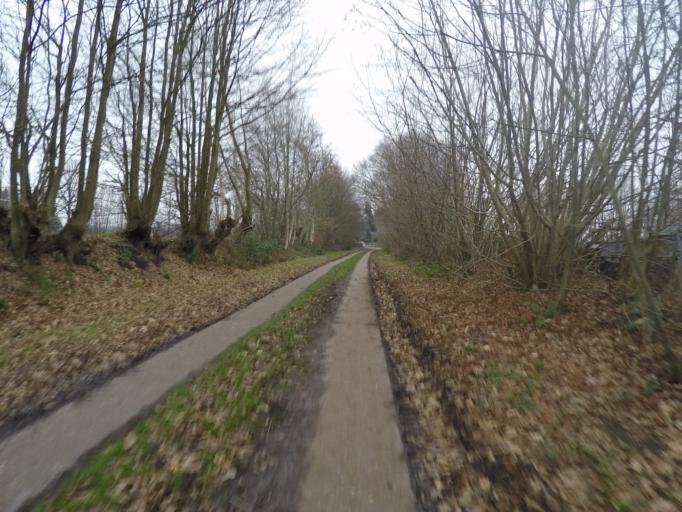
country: DE
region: Schleswig-Holstein
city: Borstel-Hohenraden
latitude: 53.6956
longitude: 9.8297
